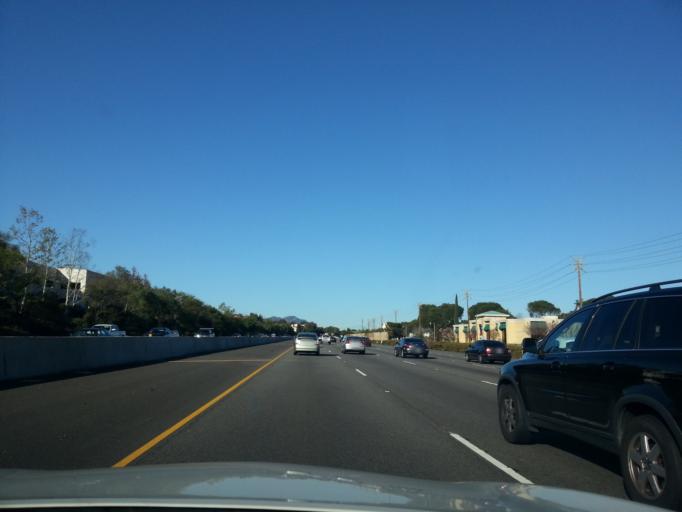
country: US
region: California
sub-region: Los Angeles County
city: Agoura Hills
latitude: 34.1466
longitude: -118.7865
